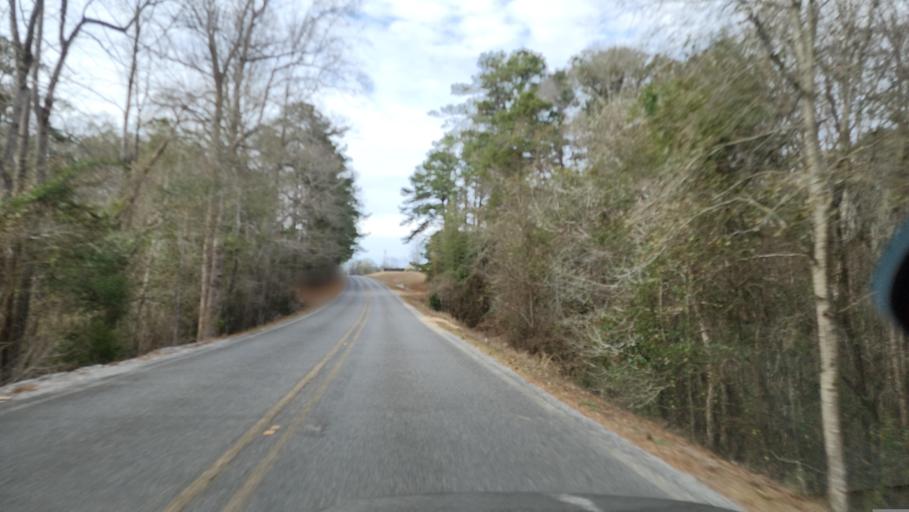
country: US
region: Mississippi
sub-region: Clarke County
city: Stonewall
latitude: 32.1986
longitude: -88.6841
